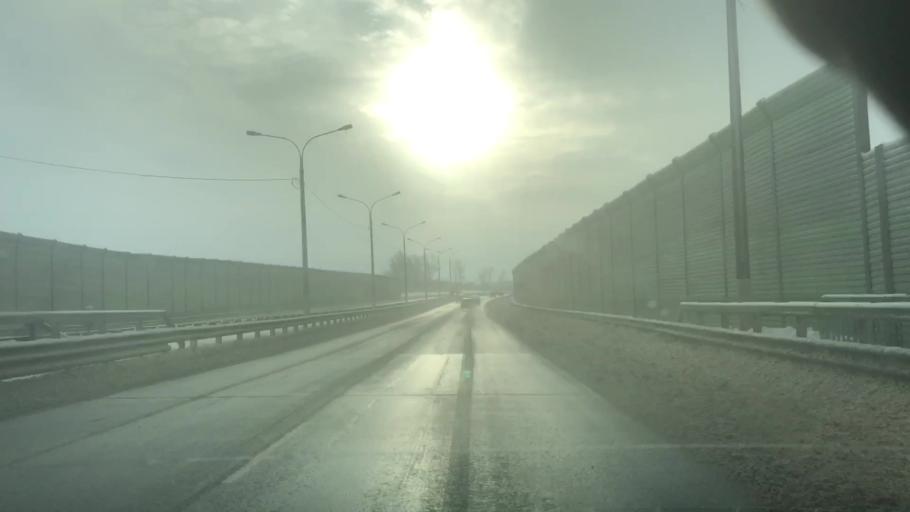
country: RU
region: Tula
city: Venev
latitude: 54.2769
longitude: 38.1601
